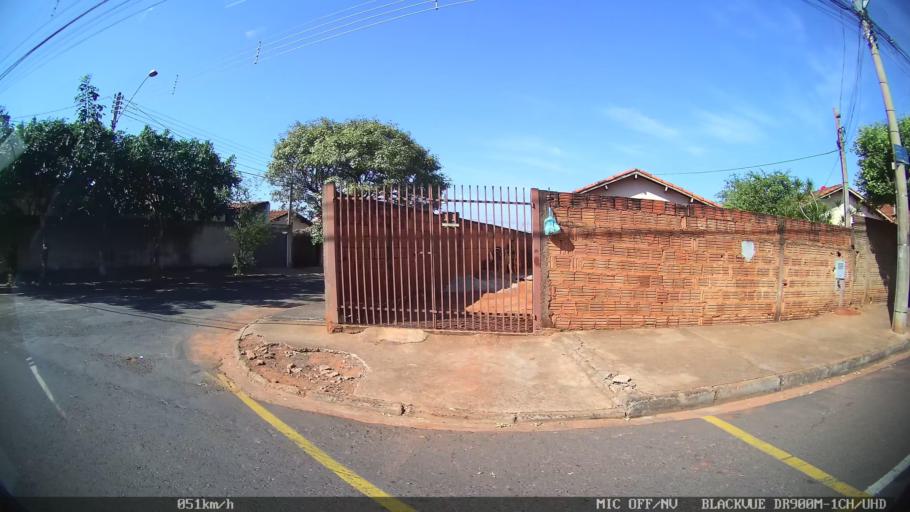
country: BR
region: Sao Paulo
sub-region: Sao Jose Do Rio Preto
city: Sao Jose do Rio Preto
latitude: -20.7662
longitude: -49.3821
